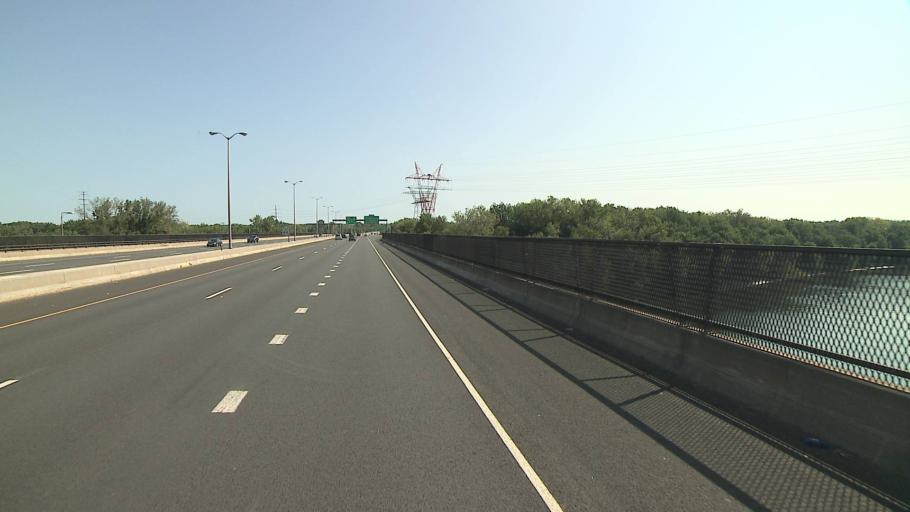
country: US
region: Connecticut
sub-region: Hartford County
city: Hartford
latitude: 41.7531
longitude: -72.6539
